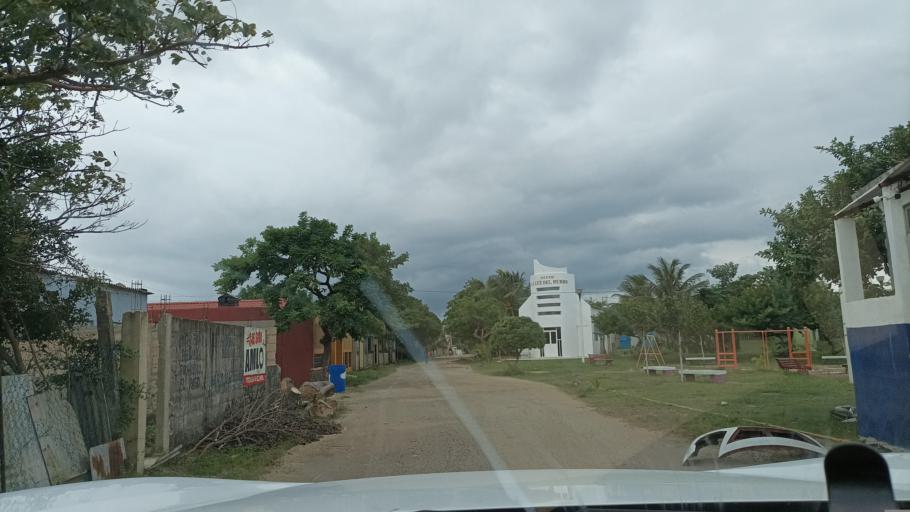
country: MX
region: Veracruz
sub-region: Coatzacoalcos
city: Fraccionamiento Ciudad Olmeca
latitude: 18.1800
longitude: -94.5891
